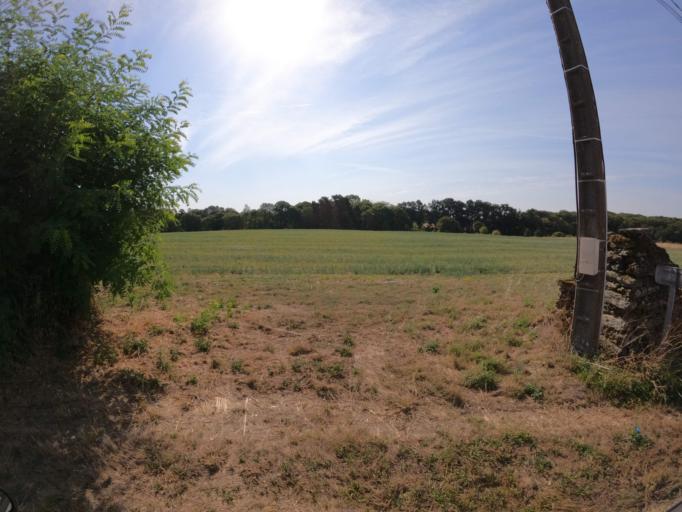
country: FR
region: Pays de la Loire
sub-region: Departement de la Vendee
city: Saint-Christophe-du-Ligneron
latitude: 46.8297
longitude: -1.7586
